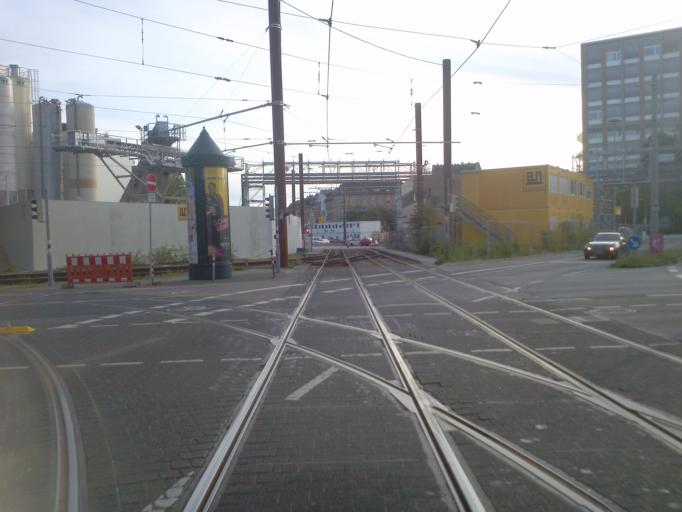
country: DE
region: Baden-Wuerttemberg
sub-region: Karlsruhe Region
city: Karlsruhe
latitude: 49.0097
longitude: 8.4188
